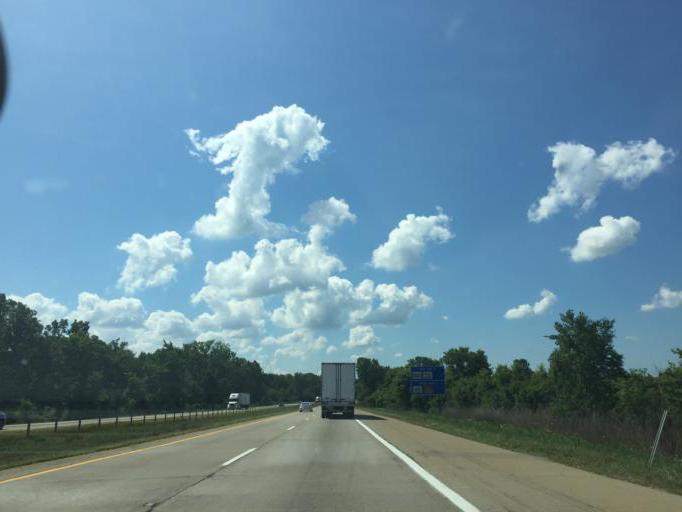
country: US
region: Michigan
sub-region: Monroe County
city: Lambertville
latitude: 41.8097
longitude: -83.6840
